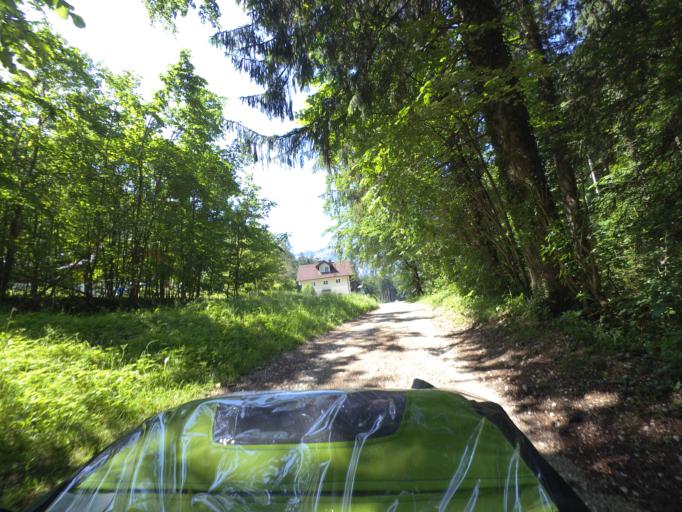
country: DE
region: Bavaria
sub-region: Upper Bavaria
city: Bayerisch Gmain
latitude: 47.7242
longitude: 12.9352
